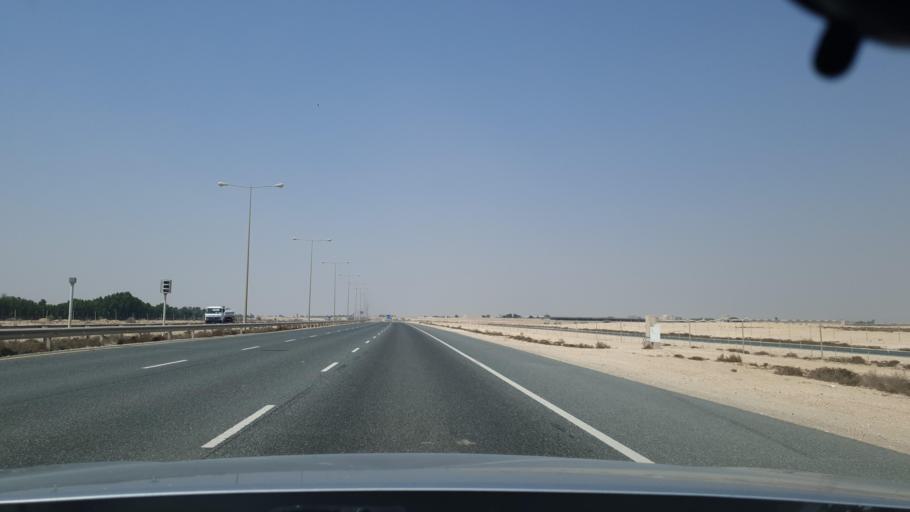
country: QA
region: Al Khawr
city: Al Khawr
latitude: 25.7758
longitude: 51.4089
